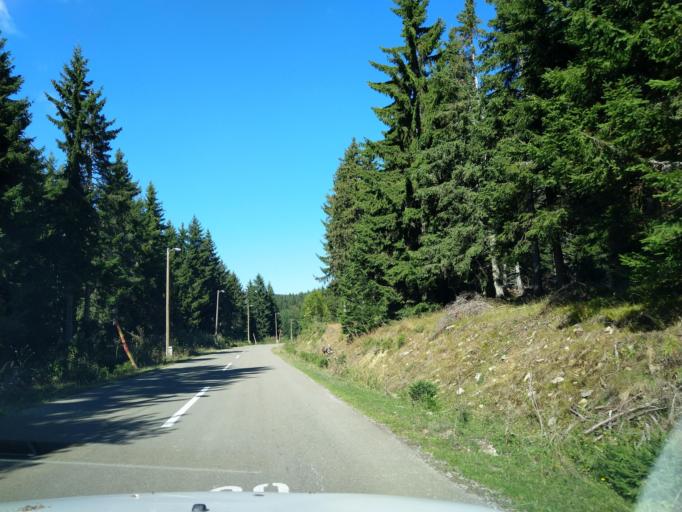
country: RS
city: Sokolovica
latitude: 43.2717
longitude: 20.3479
